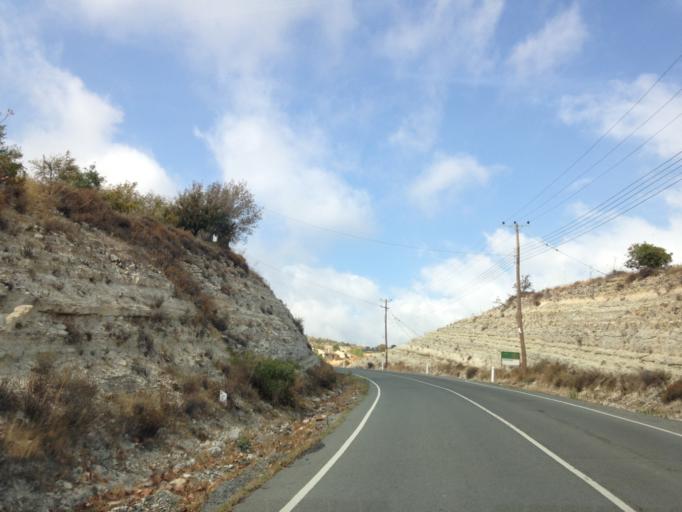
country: CY
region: Limassol
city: Pachna
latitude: 34.8231
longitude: 32.7990
